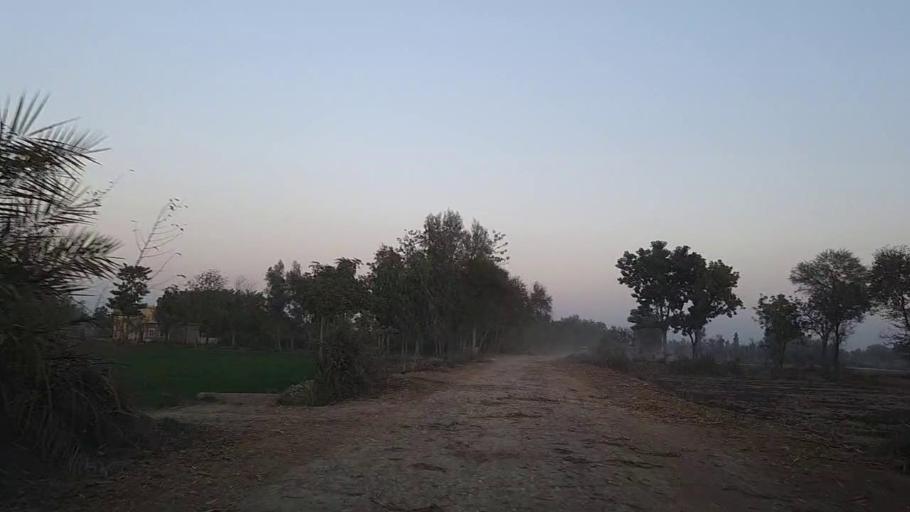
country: PK
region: Sindh
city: Naushahro Firoz
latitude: 26.7997
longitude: 68.0300
